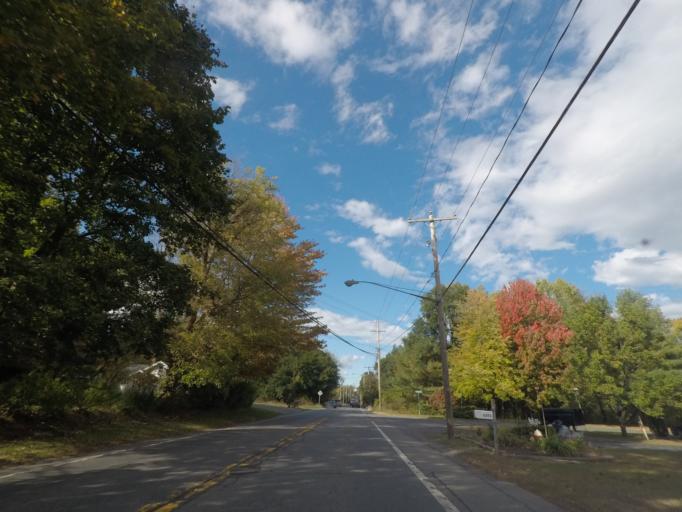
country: US
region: New York
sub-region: Schenectady County
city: Rotterdam
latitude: 42.7493
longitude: -73.9421
